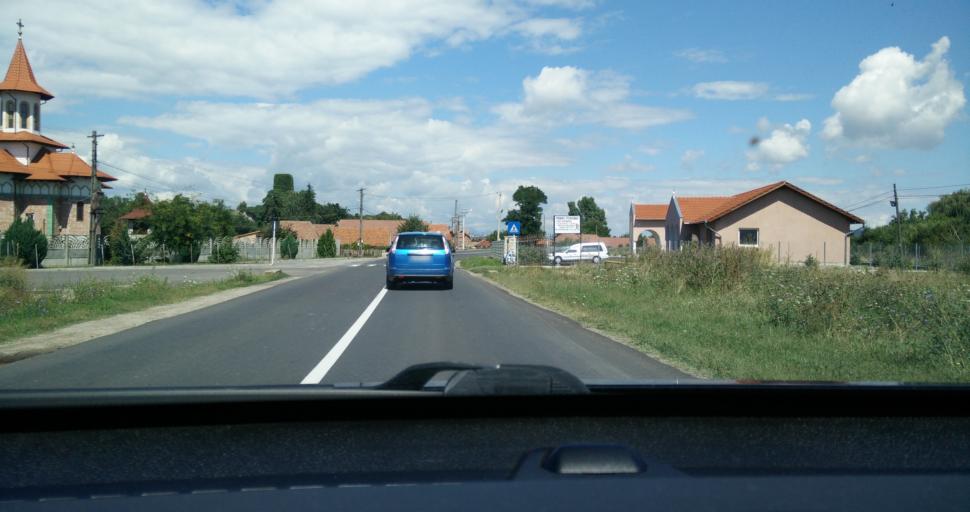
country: RO
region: Alba
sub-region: Municipiul Sebes
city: Petresti
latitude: 45.9179
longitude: 23.5557
